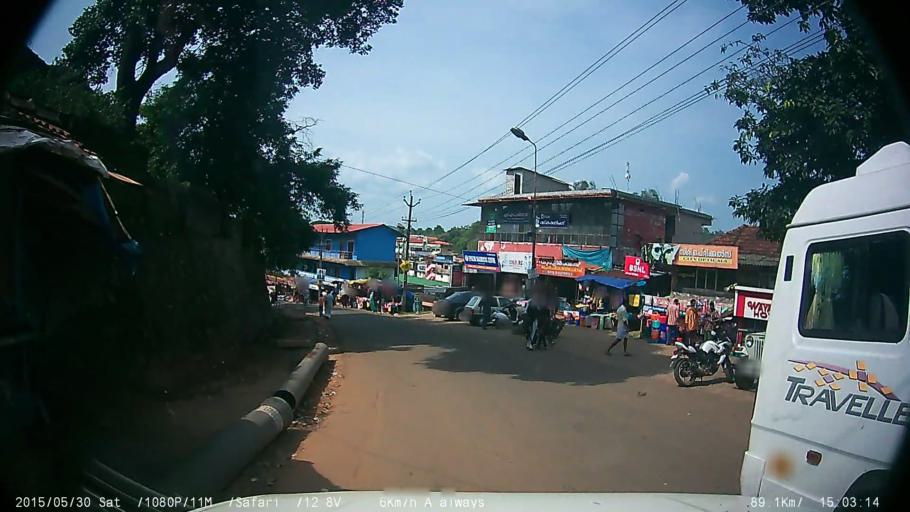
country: IN
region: Kerala
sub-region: Wayanad
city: Panamaram
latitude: 11.8008
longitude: 76.0023
